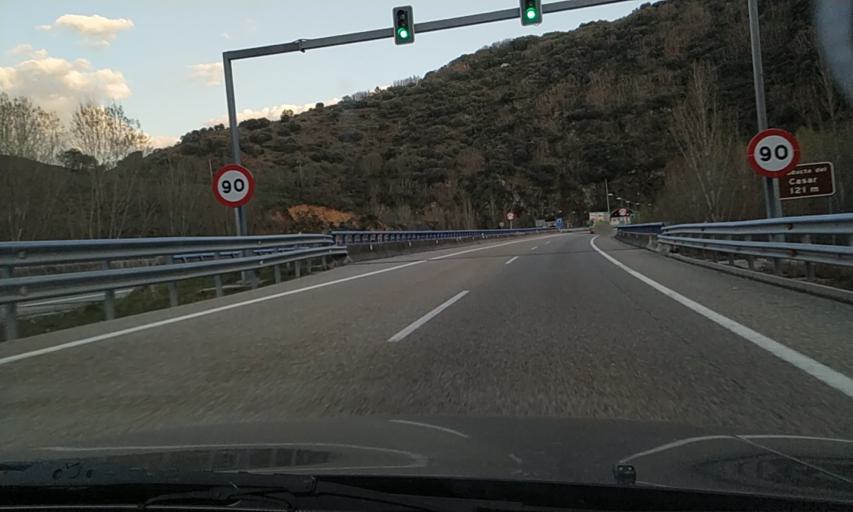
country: ES
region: Castille and Leon
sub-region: Provincia de Leon
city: Villafranca del Bierzo
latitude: 42.6131
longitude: -6.8224
